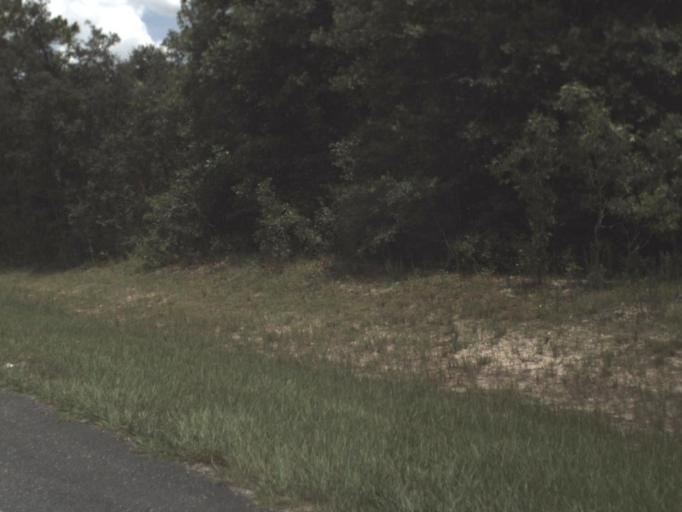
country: US
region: Florida
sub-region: Levy County
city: Williston Highlands
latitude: 29.3471
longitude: -82.5096
